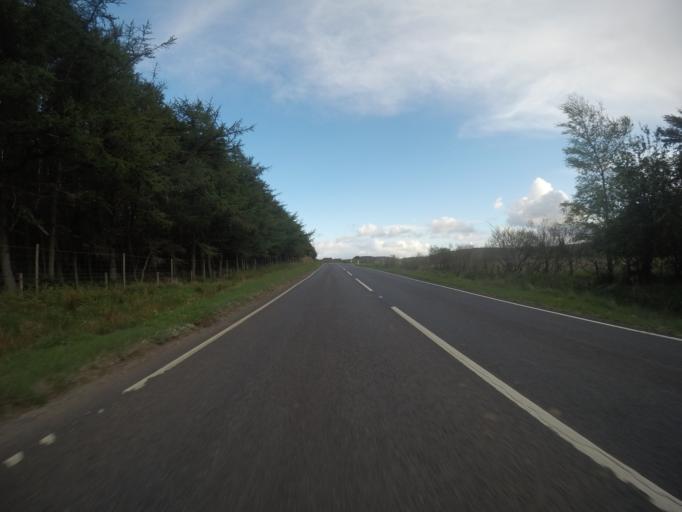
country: GB
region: Scotland
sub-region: Highland
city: Portree
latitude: 57.5289
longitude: -6.3485
